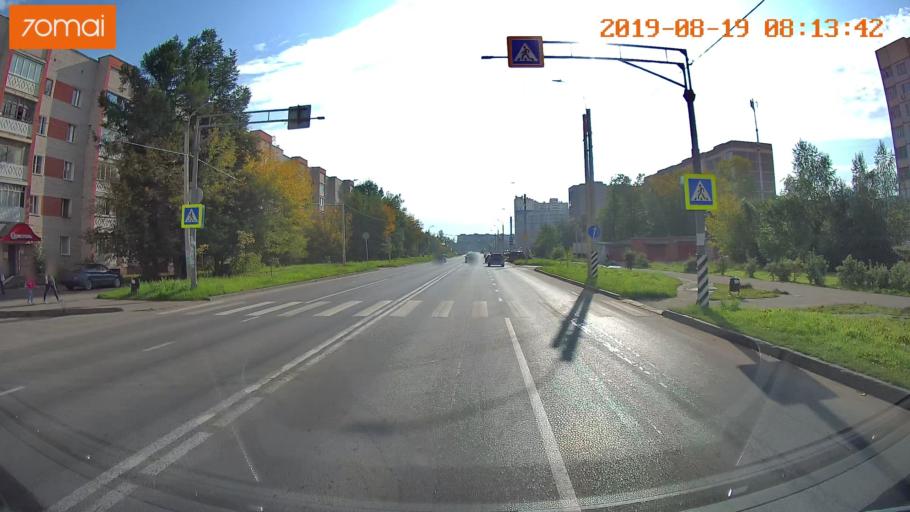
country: RU
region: Ivanovo
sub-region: Gorod Ivanovo
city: Ivanovo
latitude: 56.9715
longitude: 40.9798
